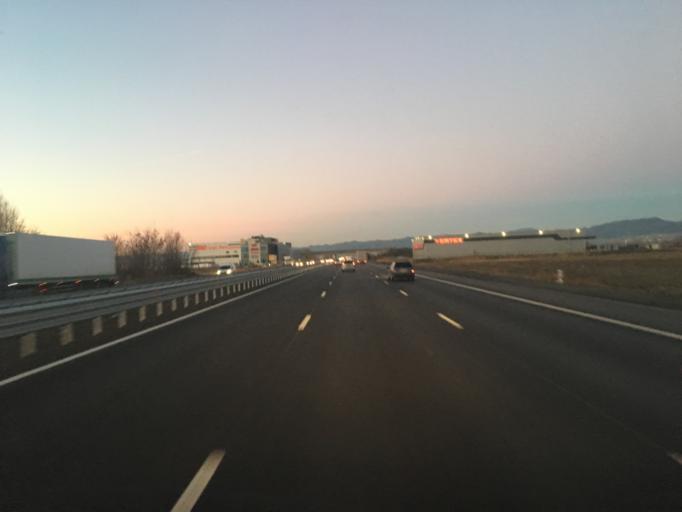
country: BG
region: Sofia-Capital
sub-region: Stolichna Obshtina
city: Sofia
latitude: 42.6827
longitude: 23.4541
